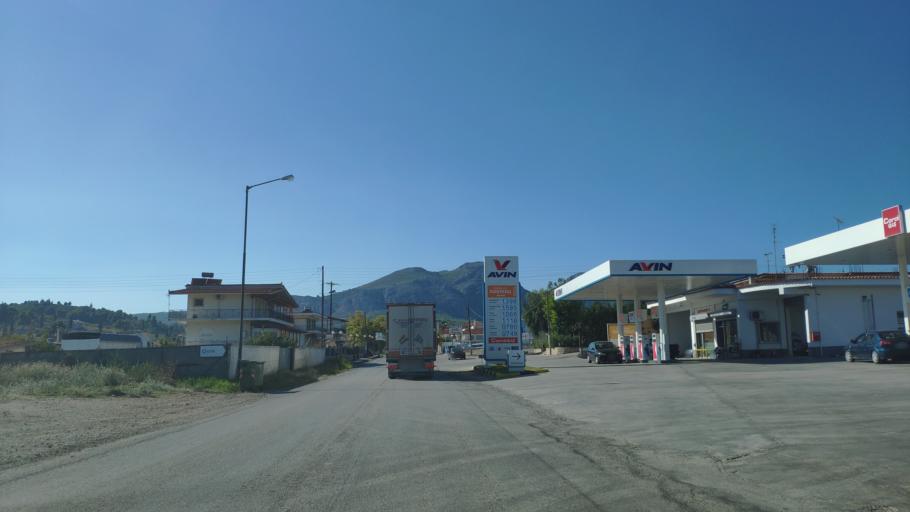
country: GR
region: Peloponnese
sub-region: Nomos Korinthias
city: Arkhaia Korinthos
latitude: 37.8826
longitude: 22.8916
